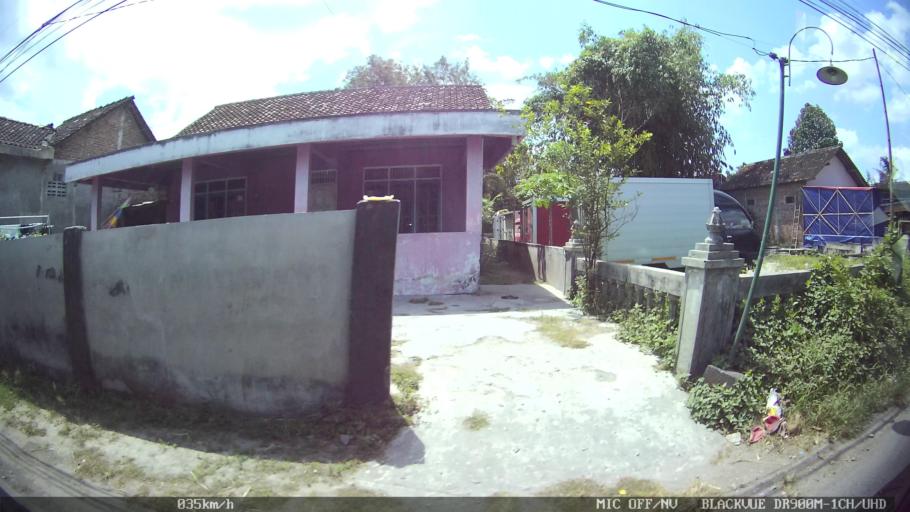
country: ID
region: Daerah Istimewa Yogyakarta
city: Sewon
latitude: -7.8732
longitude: 110.3700
